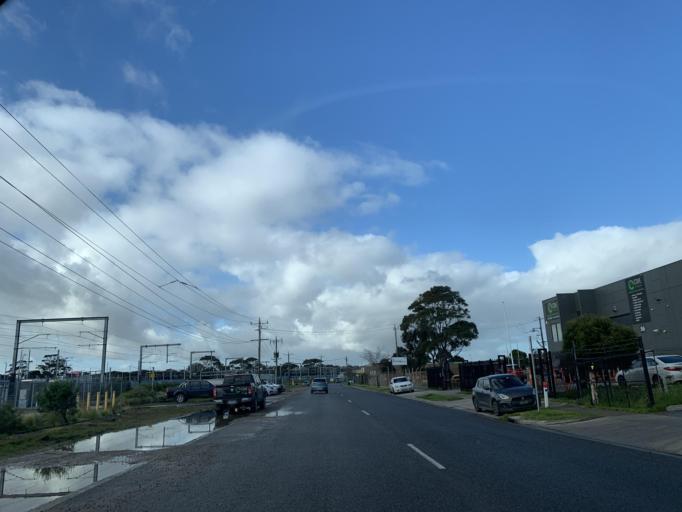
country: AU
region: Victoria
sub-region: Frankston
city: Seaford
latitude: -38.1149
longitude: 145.1337
